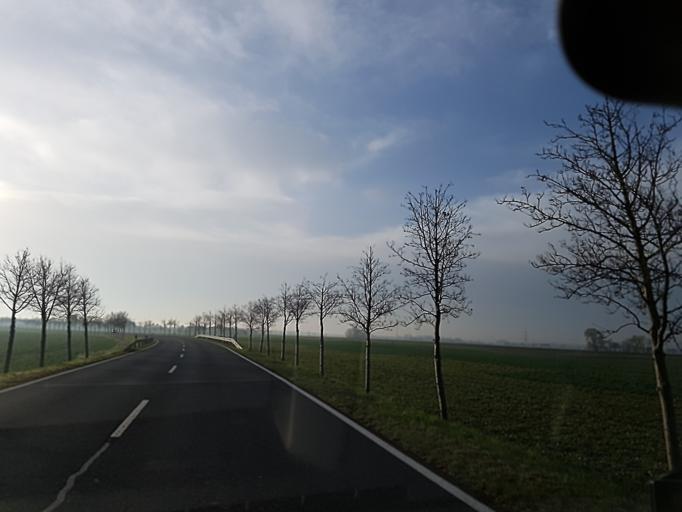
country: DE
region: Saxony
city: Strehla
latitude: 51.3519
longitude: 13.2728
